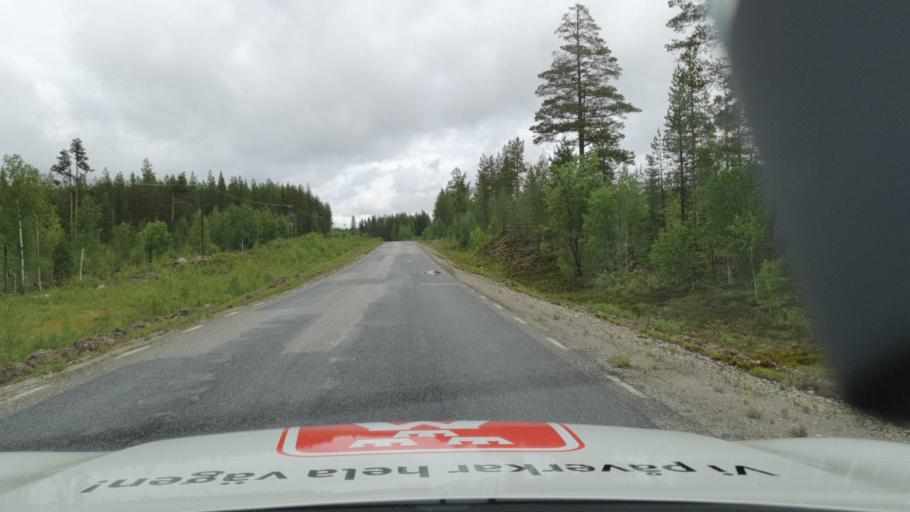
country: SE
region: Vaesterbotten
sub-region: Dorotea Kommun
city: Dorotea
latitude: 64.1362
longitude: 16.6403
